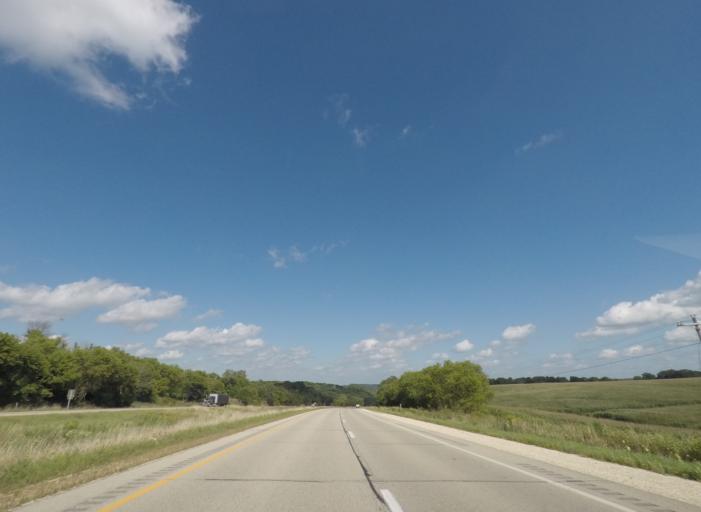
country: US
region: Iowa
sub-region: Dubuque County
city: Asbury
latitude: 42.4167
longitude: -90.7234
